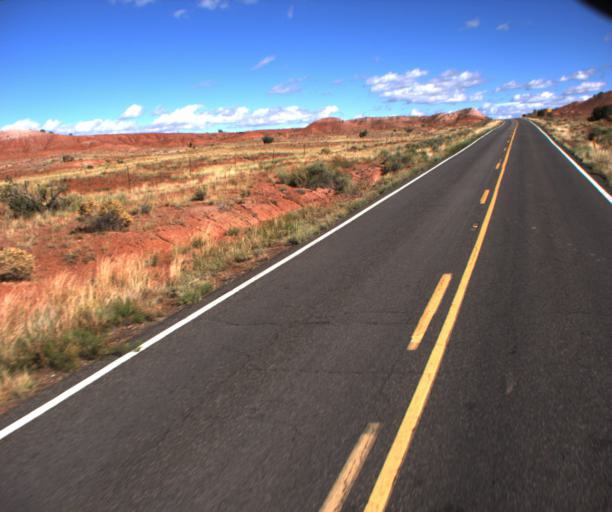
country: US
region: Arizona
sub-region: Apache County
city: Saint Johns
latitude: 34.7529
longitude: -109.2447
